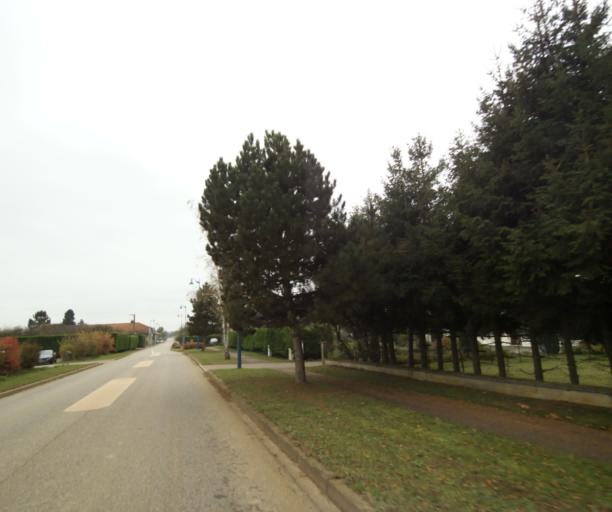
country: FR
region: Lorraine
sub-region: Departement de Meurthe-et-Moselle
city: Mancieulles
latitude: 49.2642
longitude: 5.9088
